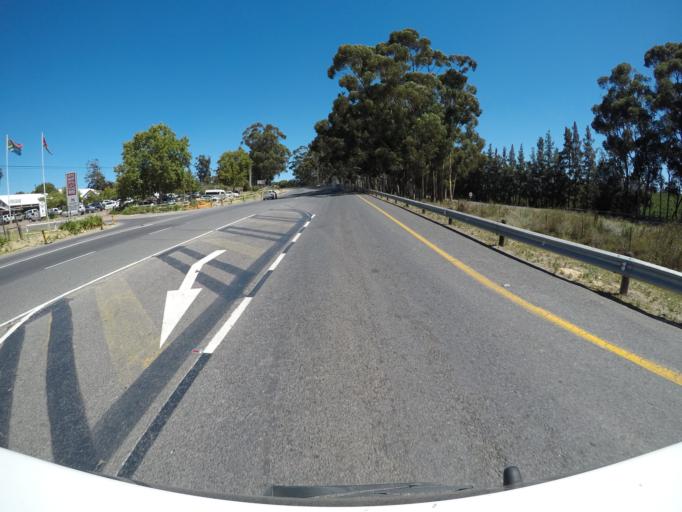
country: ZA
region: Western Cape
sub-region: Overberg District Municipality
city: Grabouw
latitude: -34.1639
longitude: 19.0355
